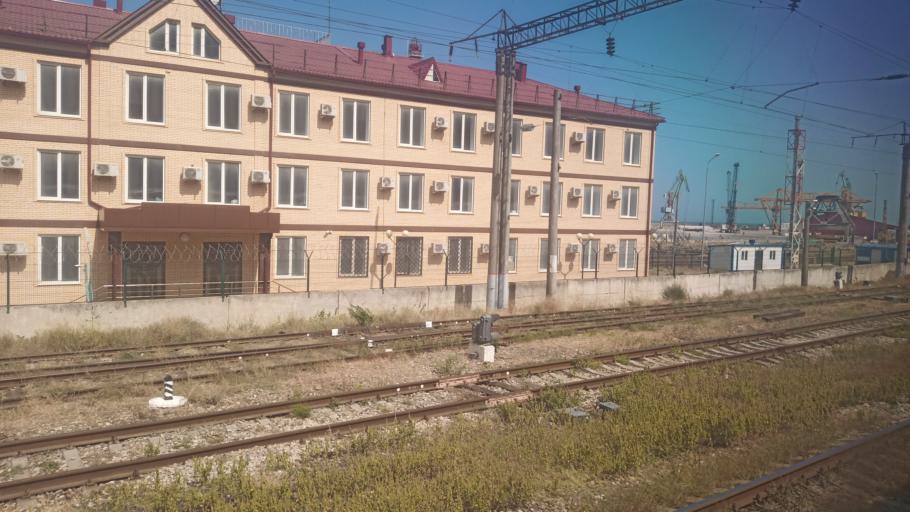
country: RU
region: Dagestan
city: Makhachkala
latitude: 42.9913
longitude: 47.4955
